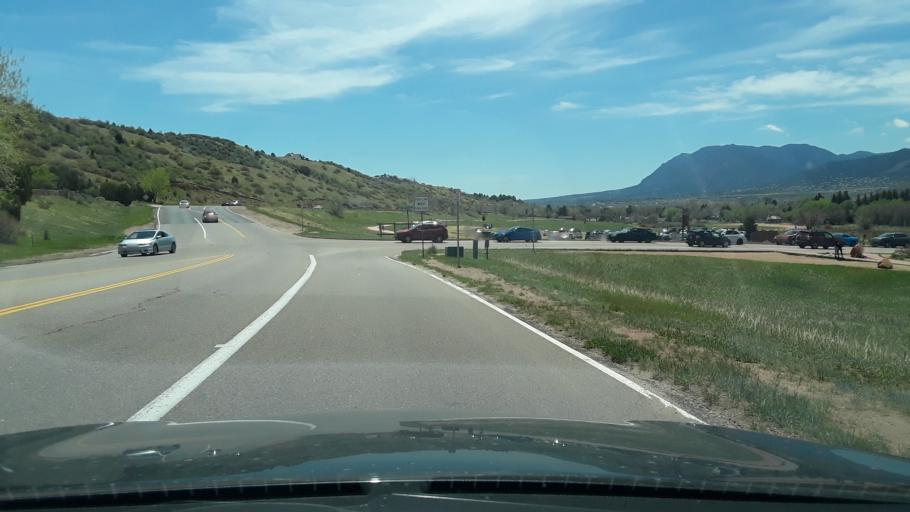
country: US
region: Colorado
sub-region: El Paso County
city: Manitou Springs
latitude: 38.8783
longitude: -104.8711
